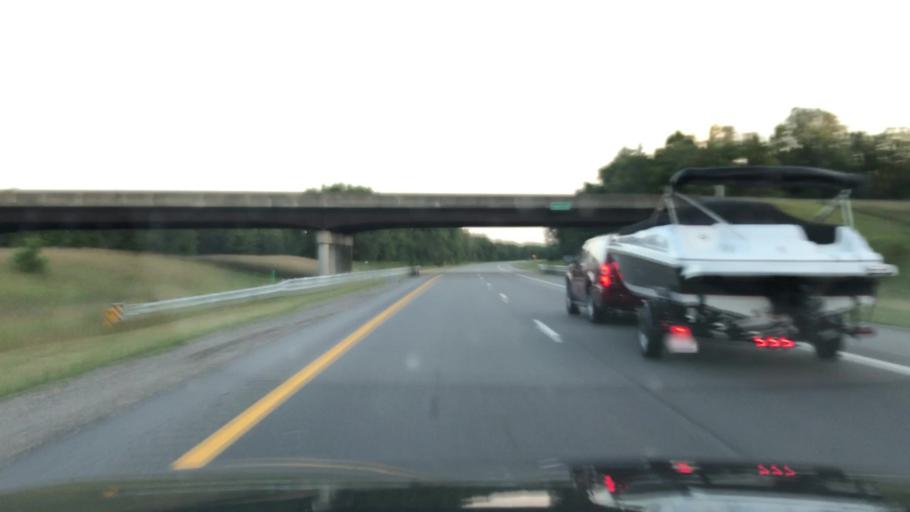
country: US
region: Michigan
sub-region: Montcalm County
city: Howard City
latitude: 43.4255
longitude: -85.4960
